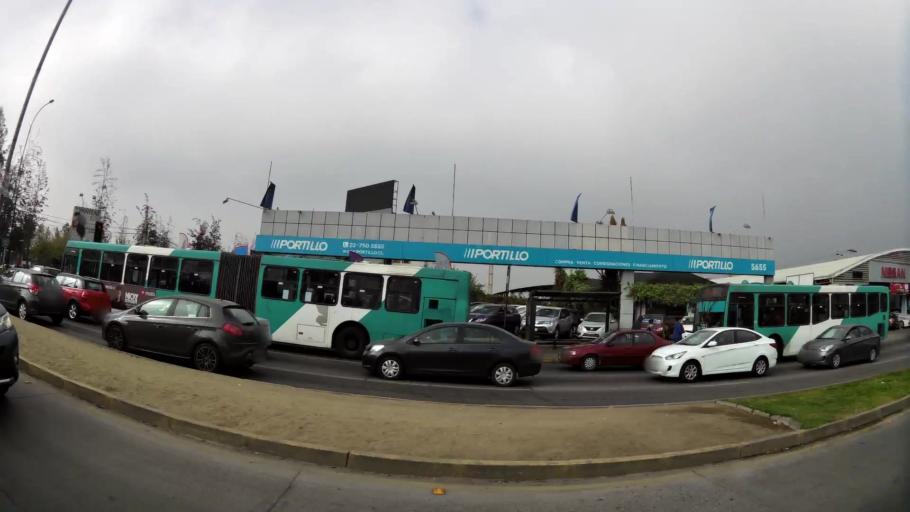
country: CL
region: Santiago Metropolitan
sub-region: Provincia de Santiago
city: Villa Presidente Frei, Nunoa, Santiago, Chile
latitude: -33.4312
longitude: -70.5753
